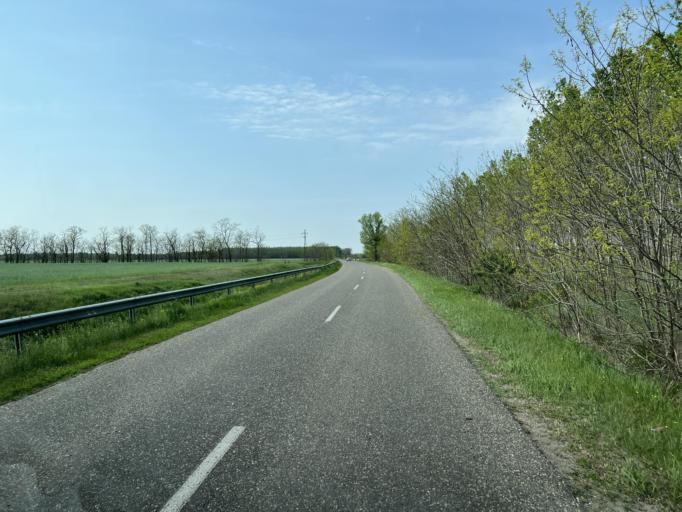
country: HU
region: Pest
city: Tortel
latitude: 47.1080
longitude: 19.9108
